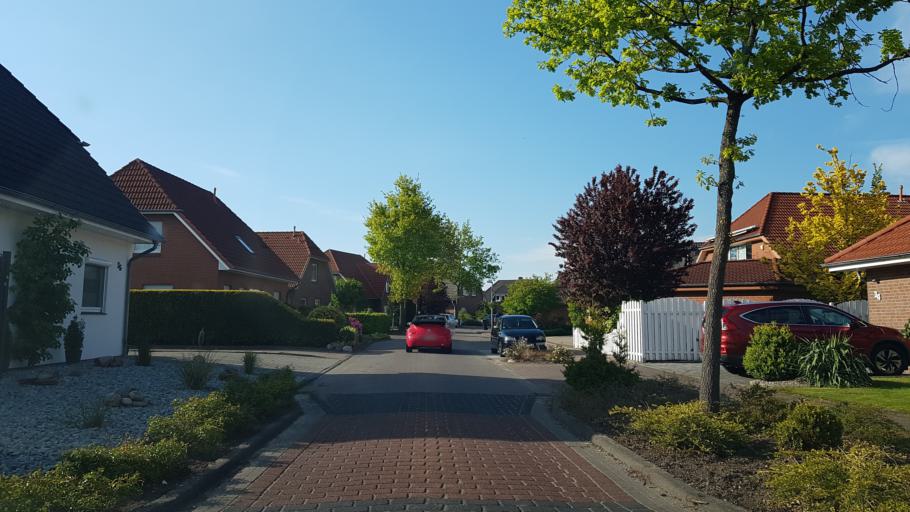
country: DE
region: Lower Saxony
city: Langen
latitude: 53.6091
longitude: 8.5900
